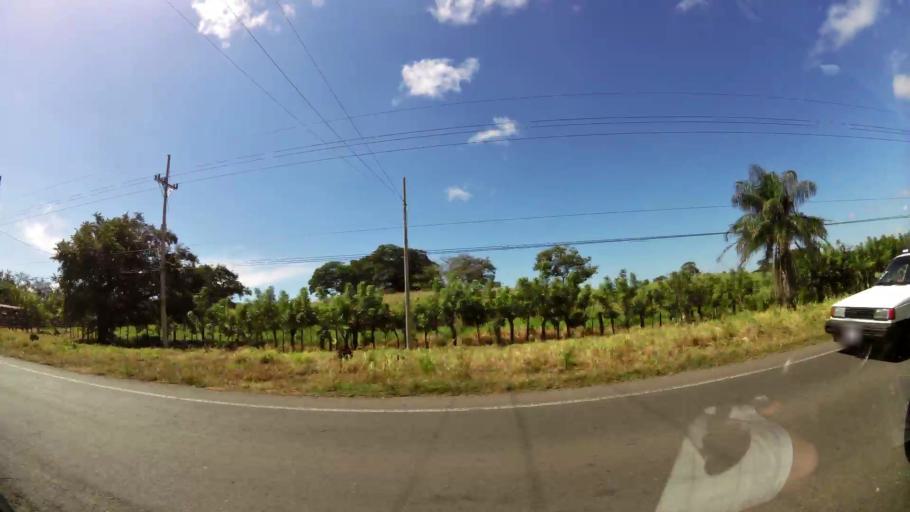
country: CR
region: Guanacaste
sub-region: Canton de Canas
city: Canas
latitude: 10.4047
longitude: -85.0860
